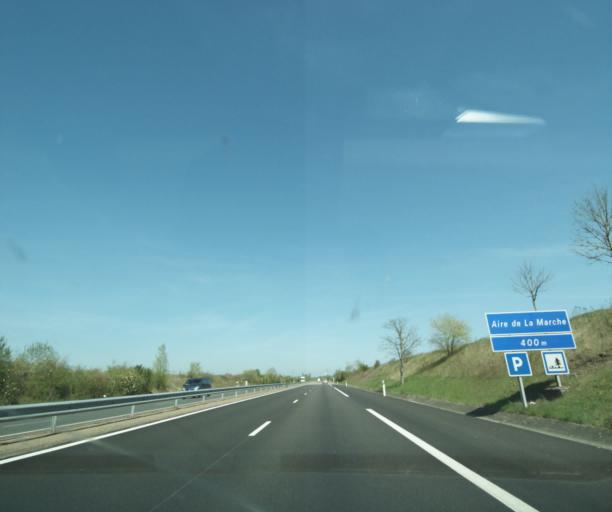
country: FR
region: Bourgogne
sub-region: Departement de la Nievre
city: La Charite-sur-Loire
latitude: 47.1507
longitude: 3.0477
